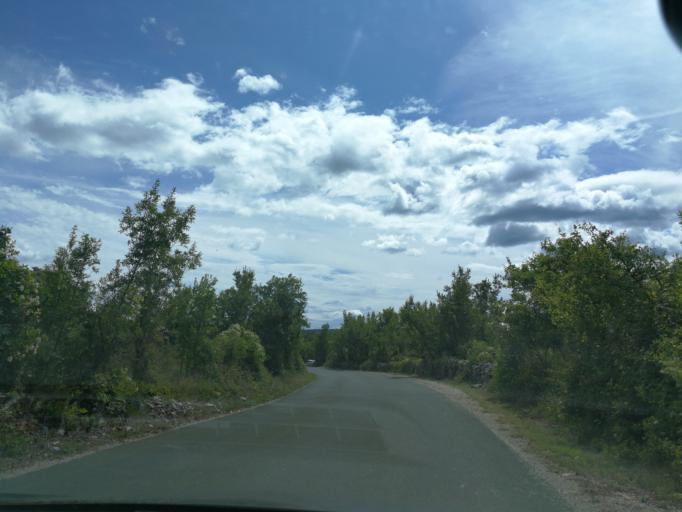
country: HR
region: Primorsko-Goranska
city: Omisalj
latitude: 45.1802
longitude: 14.5938
